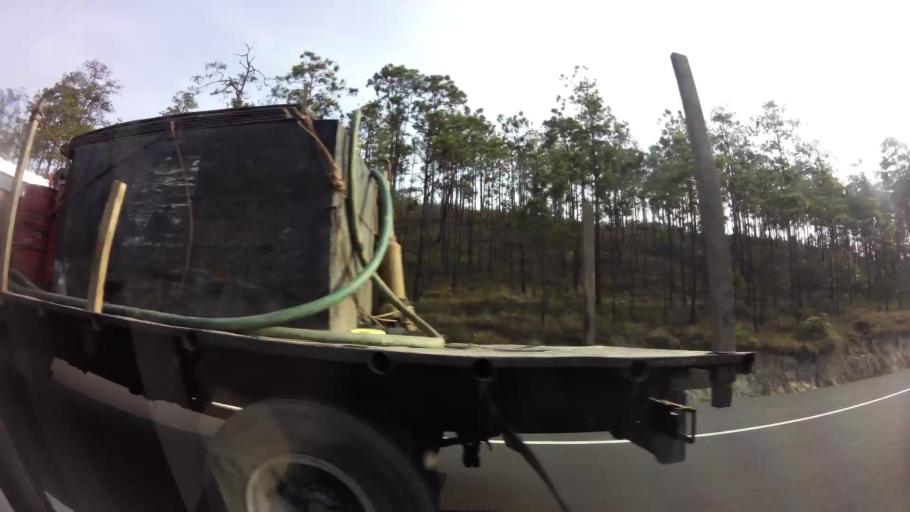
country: HN
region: Francisco Morazan
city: Zambrano
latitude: 14.2906
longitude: -87.4388
